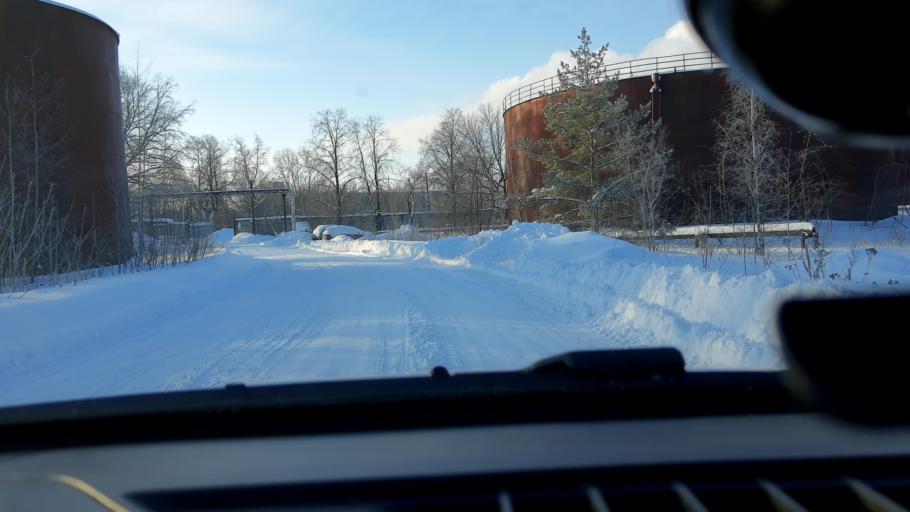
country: RU
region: Nizjnij Novgorod
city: Neklyudovo
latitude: 56.3519
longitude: 43.9093
